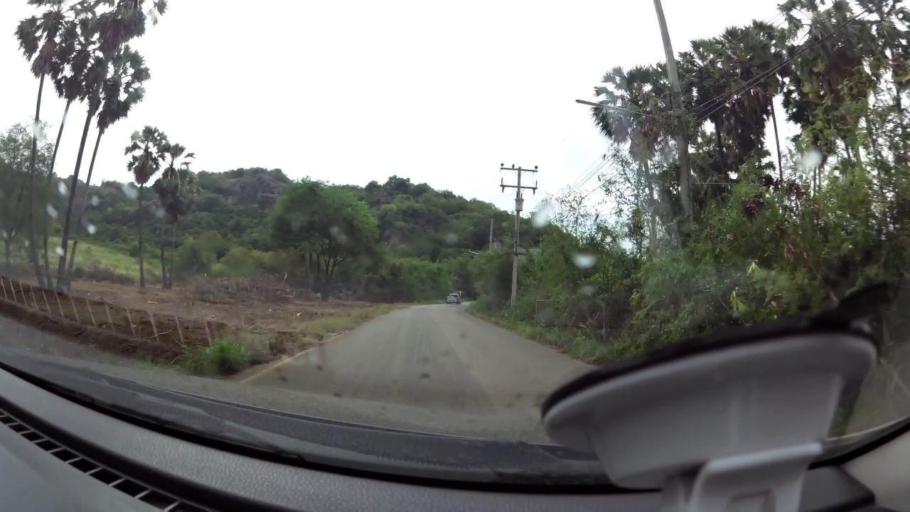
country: TH
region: Prachuap Khiri Khan
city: Pran Buri
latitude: 12.4285
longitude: 99.9787
